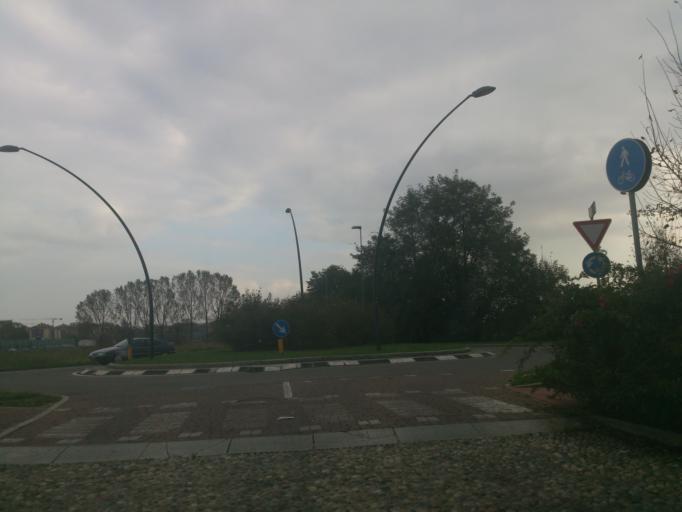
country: IT
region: Lombardy
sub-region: Citta metropolitana di Milano
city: Chiaravalle
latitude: 45.4123
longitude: 9.2531
